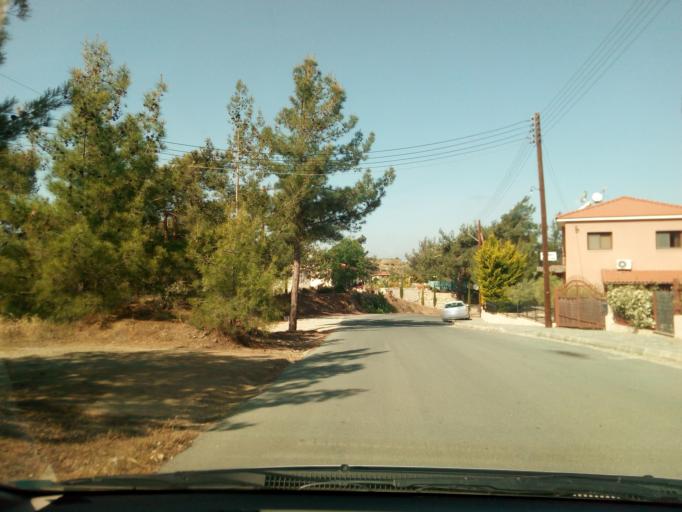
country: CY
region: Limassol
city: Pelendri
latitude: 34.8311
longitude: 33.0392
